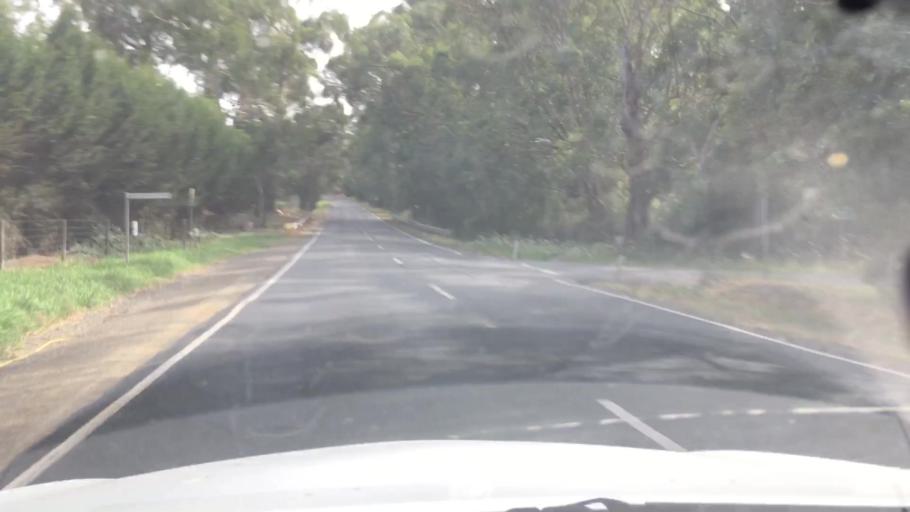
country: AU
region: Victoria
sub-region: Yarra Ranges
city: Woori Yallock
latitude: -37.8032
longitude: 145.5246
